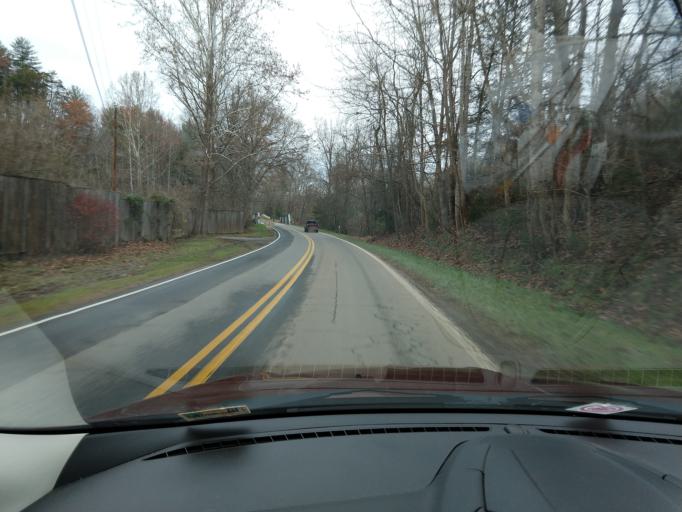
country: US
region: Virginia
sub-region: City of Covington
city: Covington
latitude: 37.7584
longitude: -80.1282
